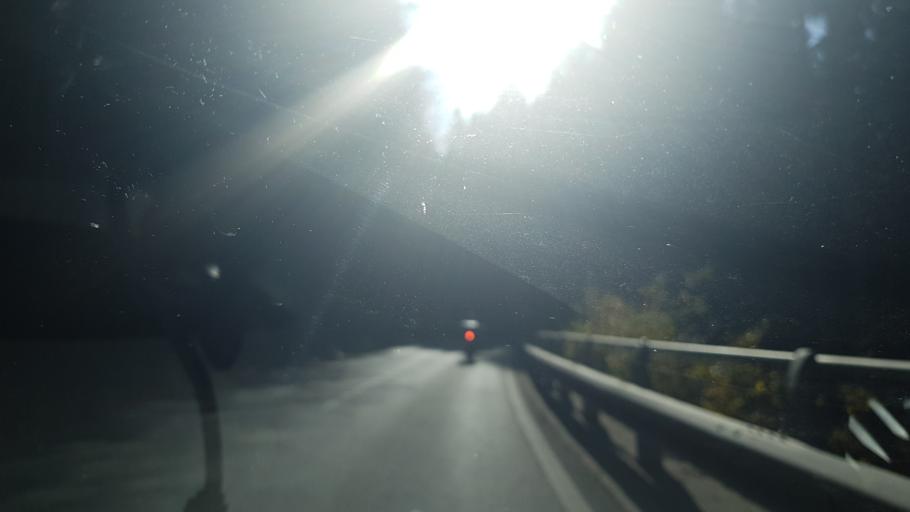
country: IT
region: Veneto
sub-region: Provincia di Belluno
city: Candide
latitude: 46.6452
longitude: 12.4514
